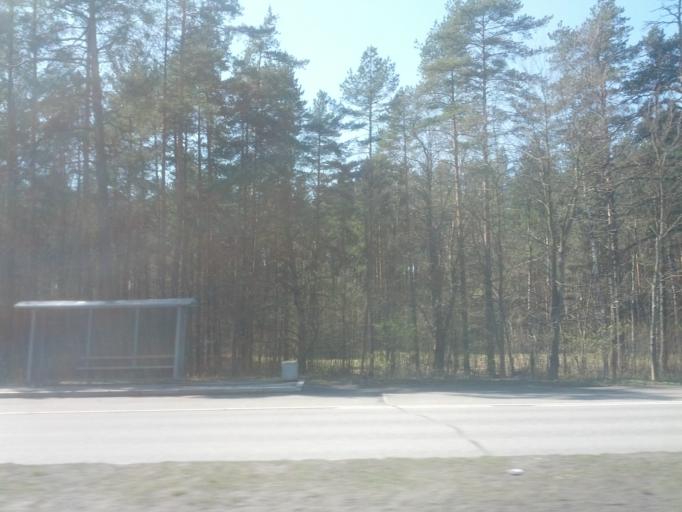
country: RU
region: St.-Petersburg
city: Tarkhovka
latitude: 60.0708
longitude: 29.9692
